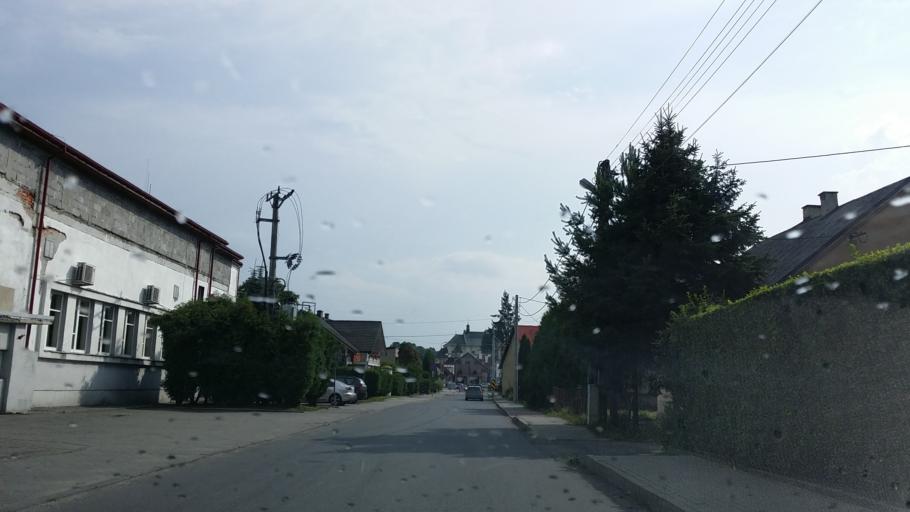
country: PL
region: Lesser Poland Voivodeship
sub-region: Powiat wadowicki
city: Spytkowice
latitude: 49.9985
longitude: 19.5125
